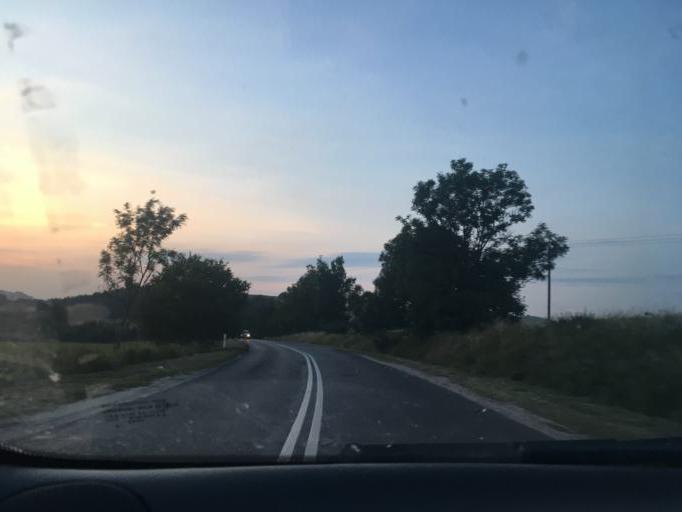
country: PL
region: Lower Silesian Voivodeship
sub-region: Powiat walbrzyski
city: Czarny Bor
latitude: 50.7713
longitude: 16.1577
